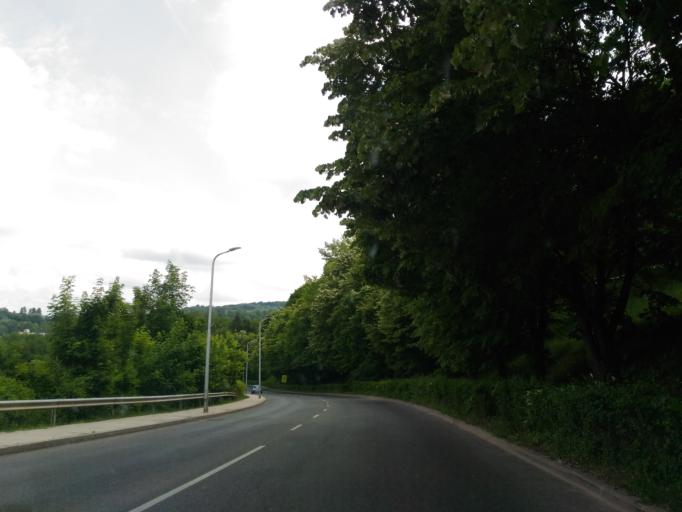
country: HU
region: Baranya
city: Komlo
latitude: 46.1877
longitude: 18.2592
